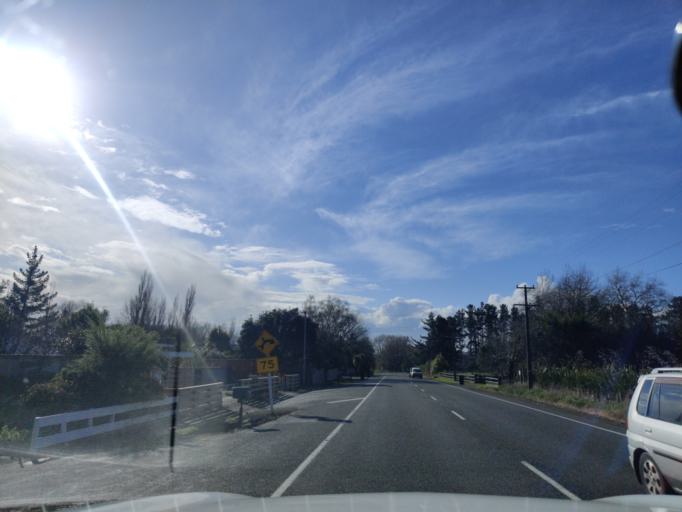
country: NZ
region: Manawatu-Wanganui
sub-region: Palmerston North City
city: Palmerston North
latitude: -40.3671
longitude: 175.6637
